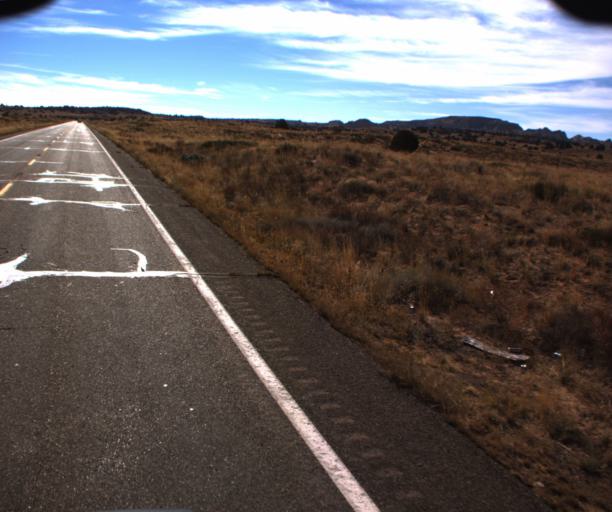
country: US
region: Arizona
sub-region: Coconino County
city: Kaibito
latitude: 36.5867
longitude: -111.1519
